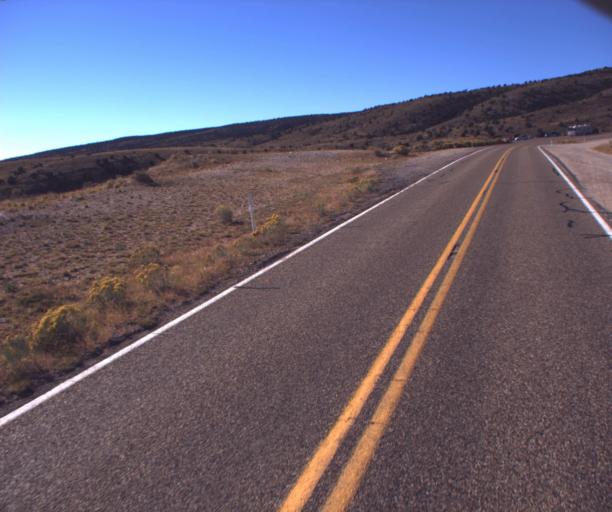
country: US
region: Arizona
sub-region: Coconino County
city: Fredonia
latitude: 36.7247
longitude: -112.0589
